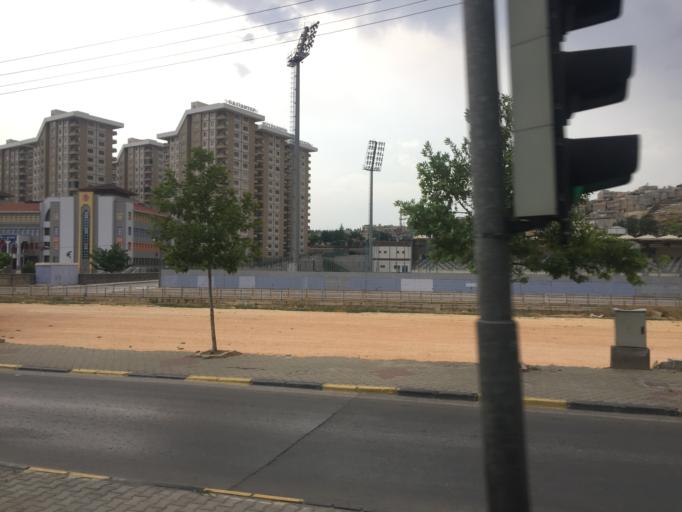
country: TR
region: Gaziantep
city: Gaziantep
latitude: 37.0746
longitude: 37.4127
